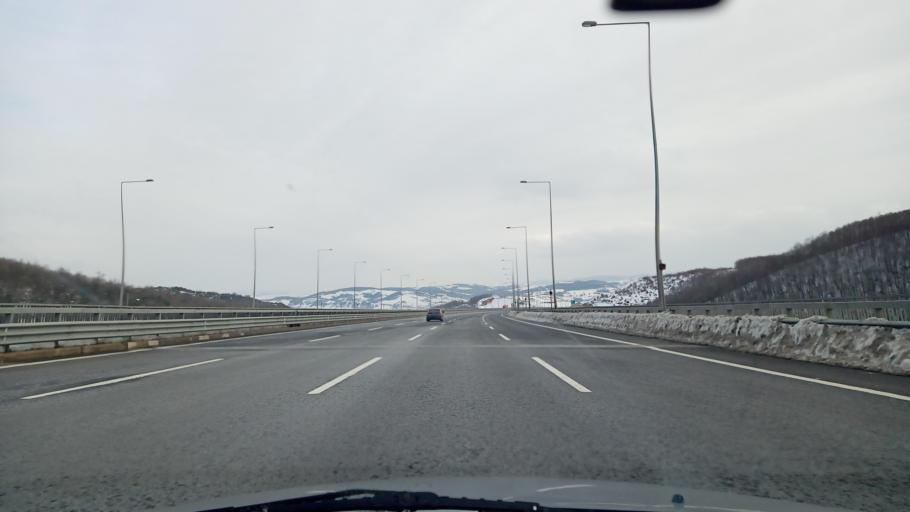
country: TR
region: Kocaeli
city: Korfez
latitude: 40.8893
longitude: 29.7272
